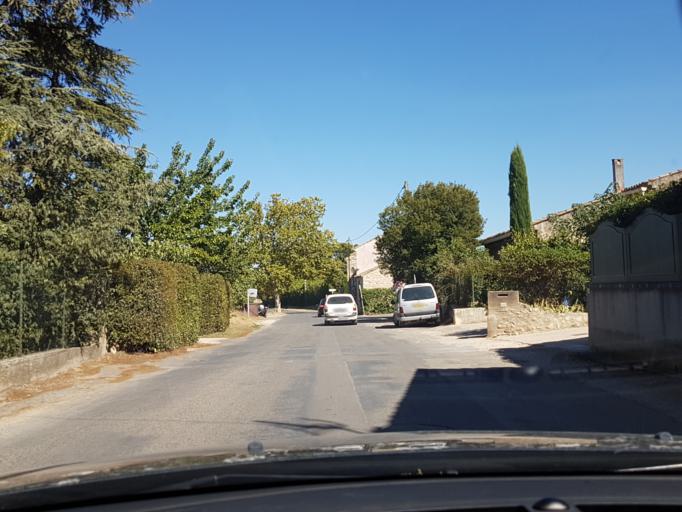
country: FR
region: Provence-Alpes-Cote d'Azur
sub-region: Departement des Bouches-du-Rhone
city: Eygalieres
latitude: 43.7606
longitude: 4.9525
